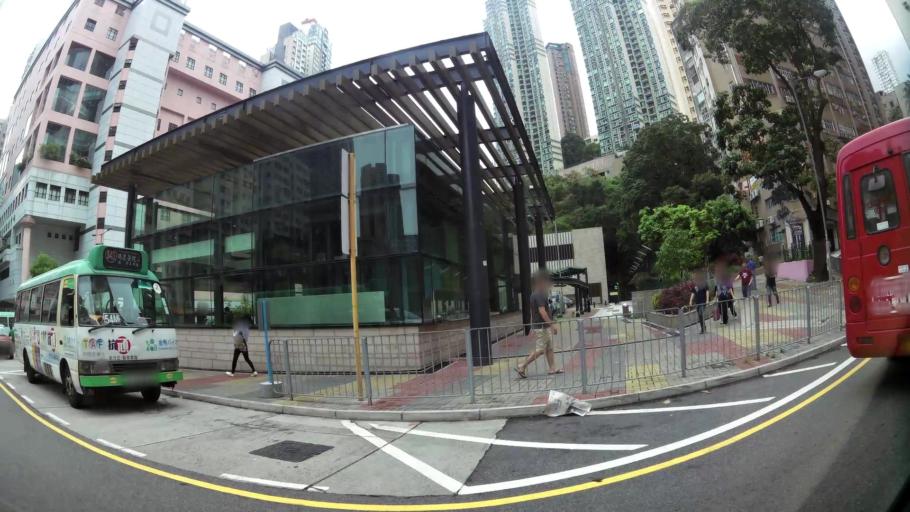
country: HK
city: Hong Kong
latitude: 22.2811
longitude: 114.1283
